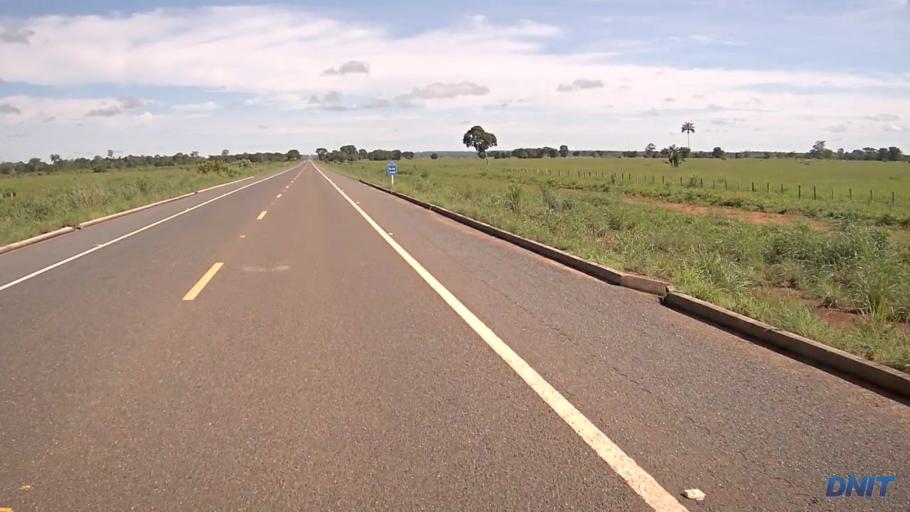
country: BR
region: Goias
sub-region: Sao Miguel Do Araguaia
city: Sao Miguel do Araguaia
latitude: -13.4253
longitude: -50.1280
